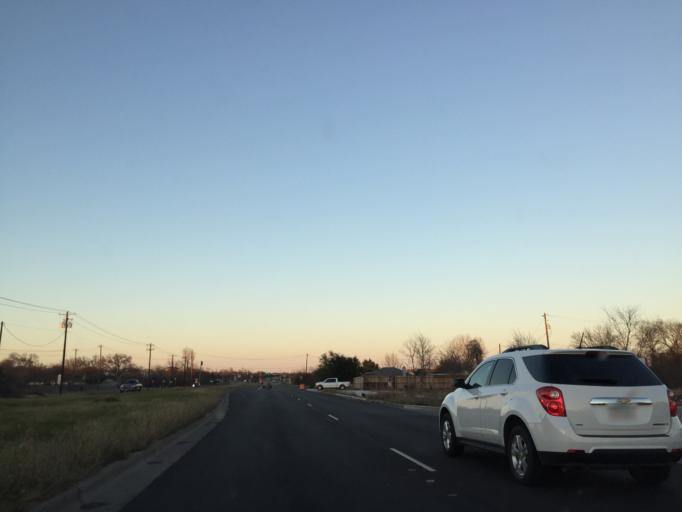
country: US
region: Texas
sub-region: Travis County
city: Pflugerville
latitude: 30.4209
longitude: -97.6287
